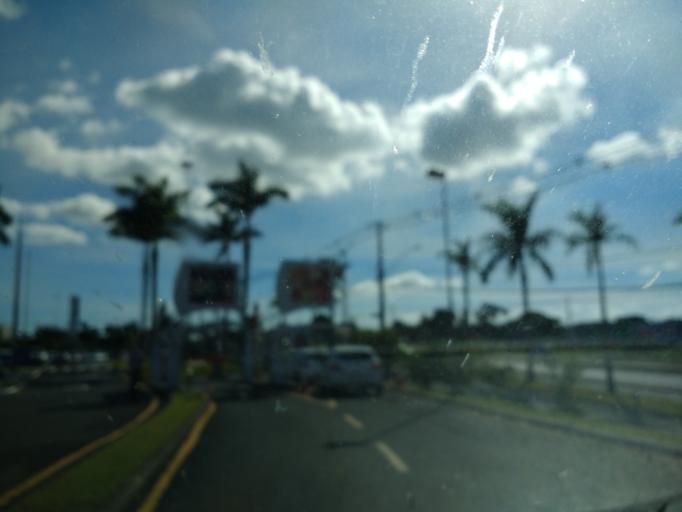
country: BR
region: Parana
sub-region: Maringa
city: Maringa
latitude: -23.4194
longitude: -51.9697
